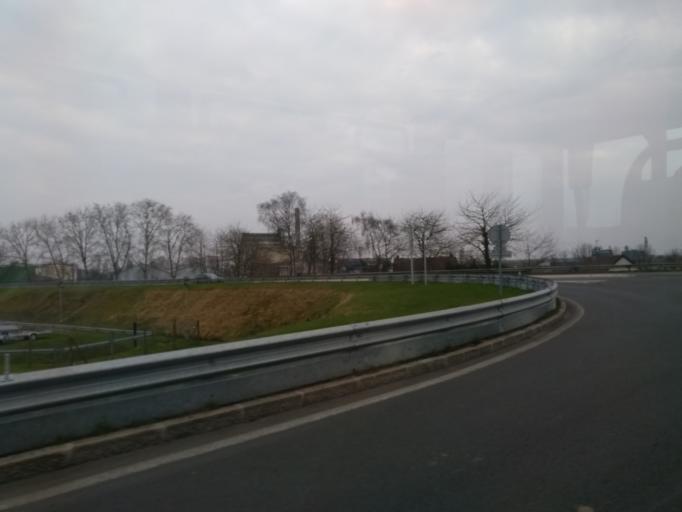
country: FR
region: Picardie
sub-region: Departement de l'Oise
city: Venette
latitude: 49.4086
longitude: 2.7924
